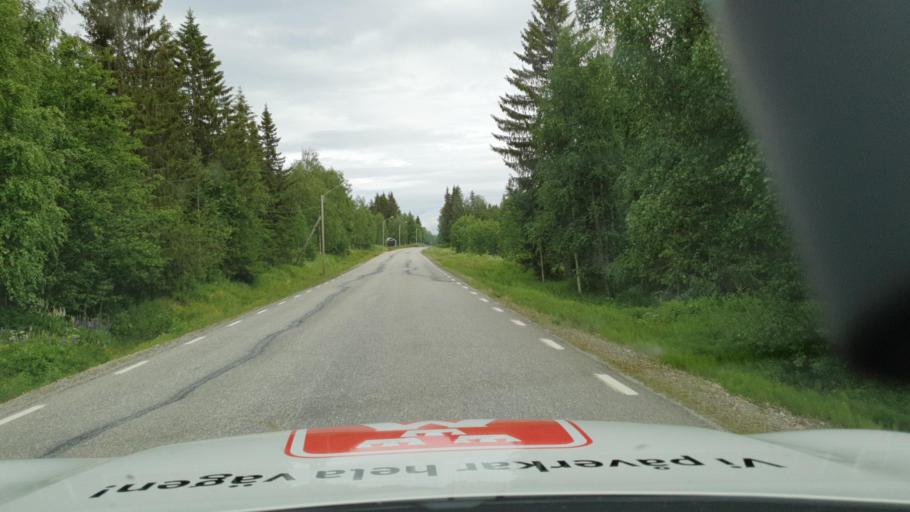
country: SE
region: Vaesterbotten
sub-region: Lycksele Kommun
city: Soderfors
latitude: 64.3627
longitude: 18.0986
